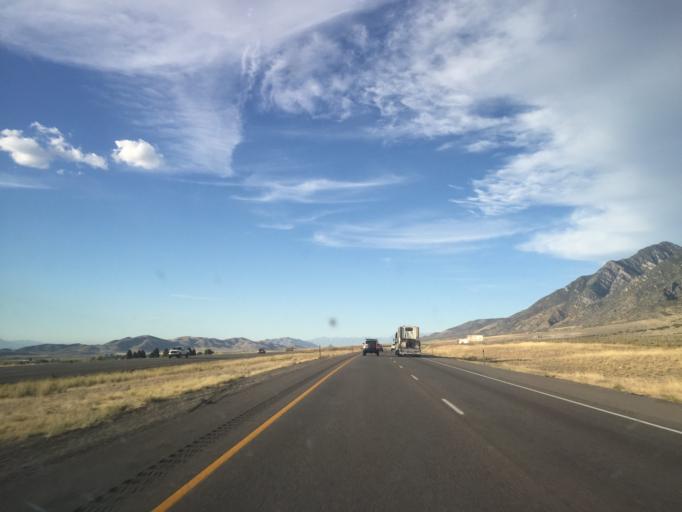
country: US
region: Utah
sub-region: Juab County
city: Mona
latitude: 39.7992
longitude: -111.8379
